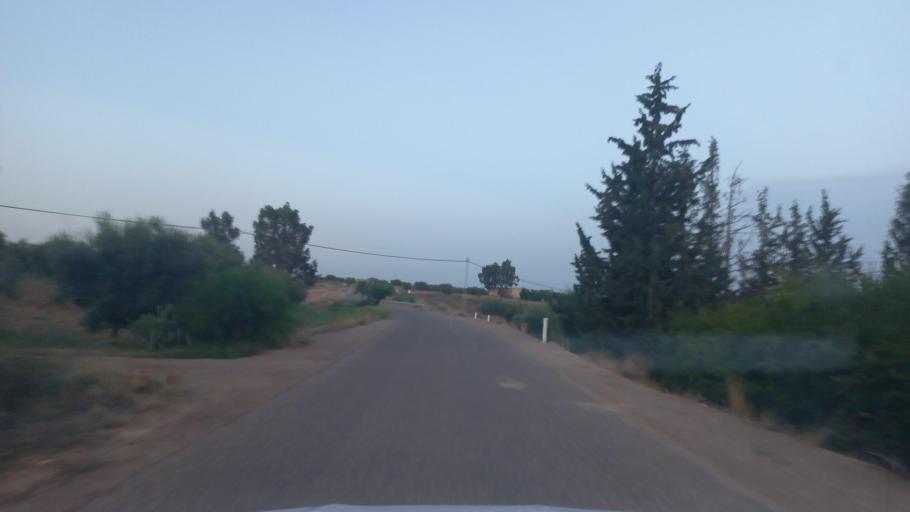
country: TN
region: Al Qasrayn
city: Kasserine
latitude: 35.2226
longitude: 9.0592
